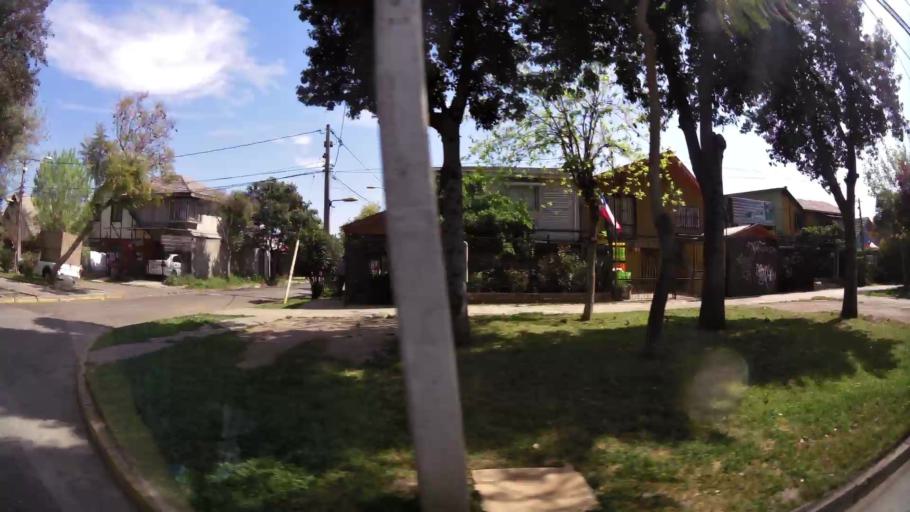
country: CL
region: Santiago Metropolitan
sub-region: Provincia de Santiago
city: Lo Prado
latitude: -33.4807
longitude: -70.7240
